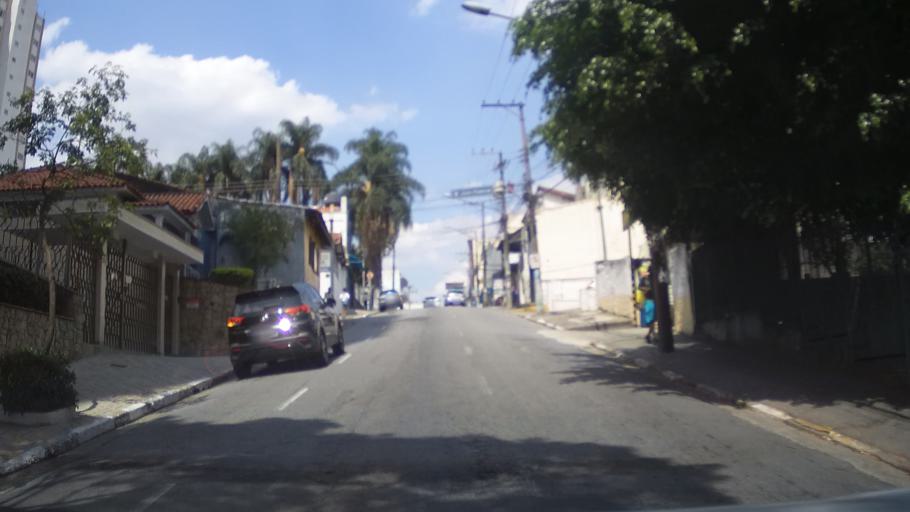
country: BR
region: Sao Paulo
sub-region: Guarulhos
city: Guarulhos
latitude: -23.4697
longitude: -46.5324
